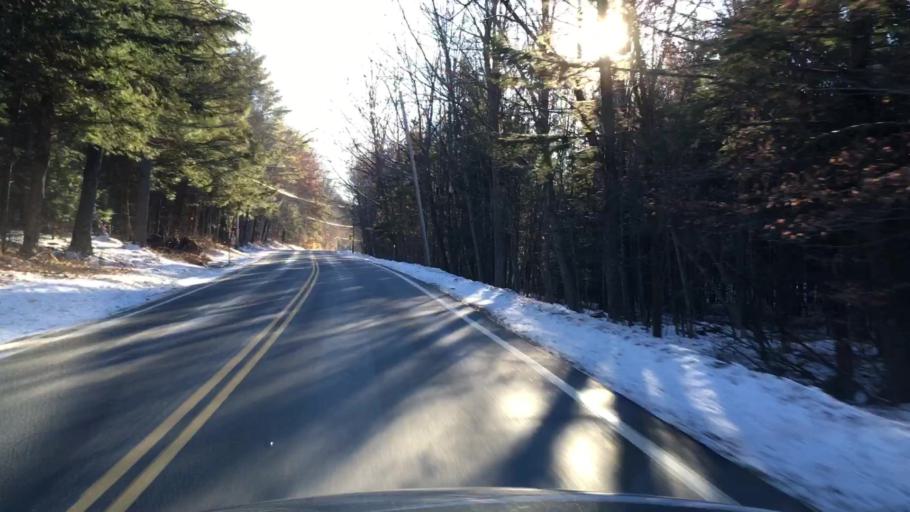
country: US
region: New Hampshire
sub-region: Grafton County
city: Woodsville
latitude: 44.2052
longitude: -72.0537
